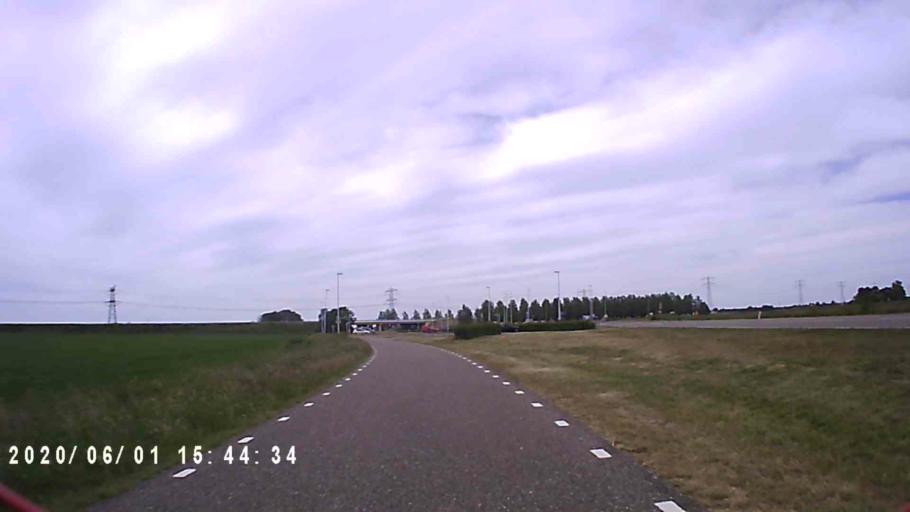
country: NL
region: Friesland
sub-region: Gemeente Boarnsterhim
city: Wergea
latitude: 53.1638
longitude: 5.8294
